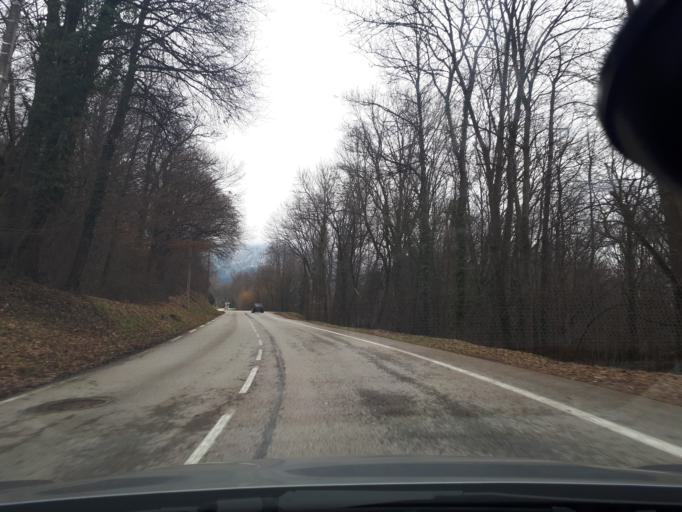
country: FR
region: Rhone-Alpes
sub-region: Departement de l'Isere
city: Vaulnaveys-le-Haut
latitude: 45.1264
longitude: 5.8269
